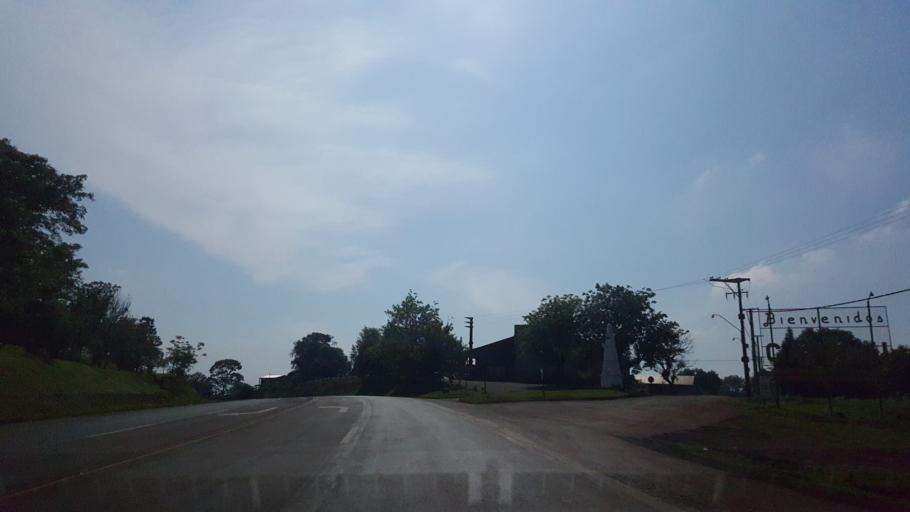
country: AR
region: Misiones
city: Capiovi
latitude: -26.9349
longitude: -55.0625
